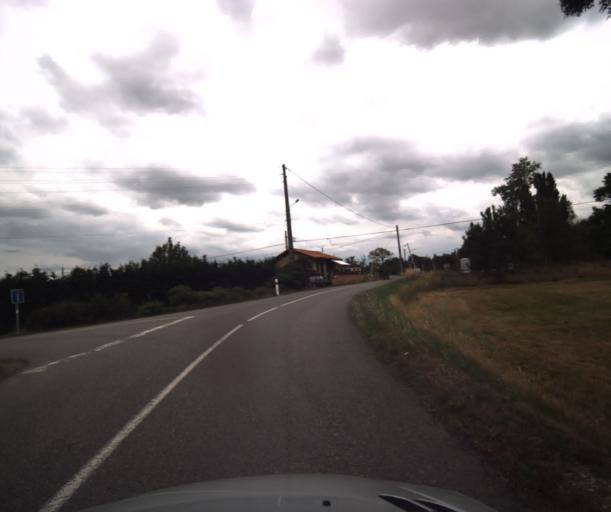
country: FR
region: Midi-Pyrenees
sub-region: Departement de la Haute-Garonne
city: Labarthe-sur-Leze
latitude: 43.4560
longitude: 1.4138
